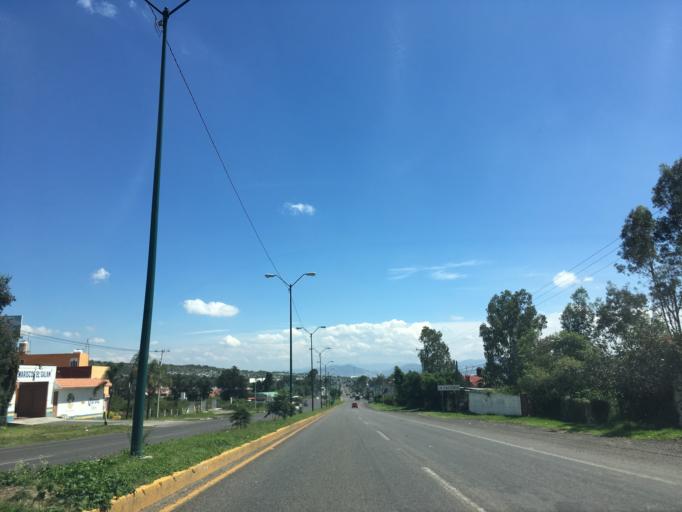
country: MX
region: Michoacan
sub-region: Morelia
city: Villa Magna
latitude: 19.6867
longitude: -101.3194
